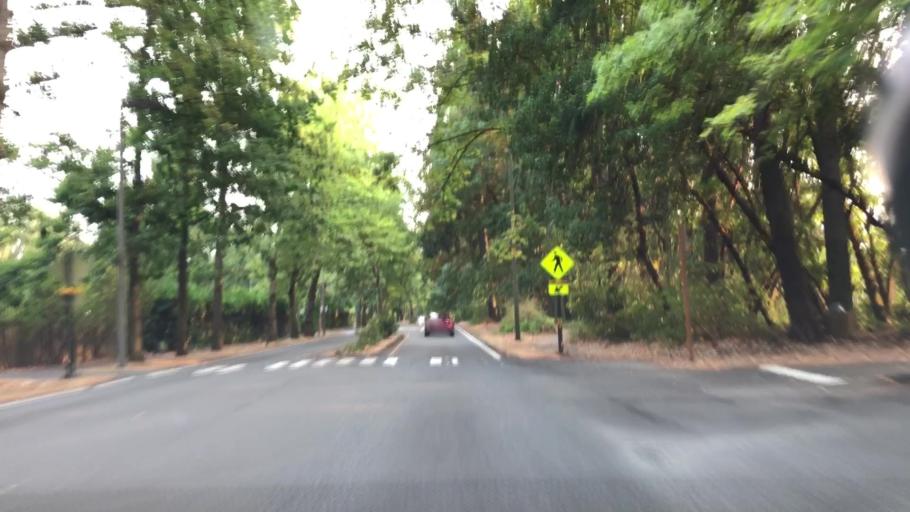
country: US
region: Washington
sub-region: King County
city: Mercer Island
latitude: 47.5516
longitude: -122.2217
